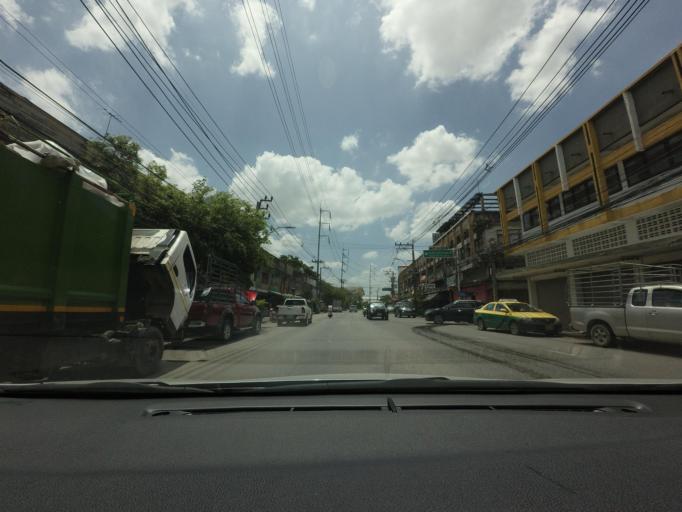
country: TH
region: Samut Prakan
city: Samut Prakan
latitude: 13.5805
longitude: 100.5927
